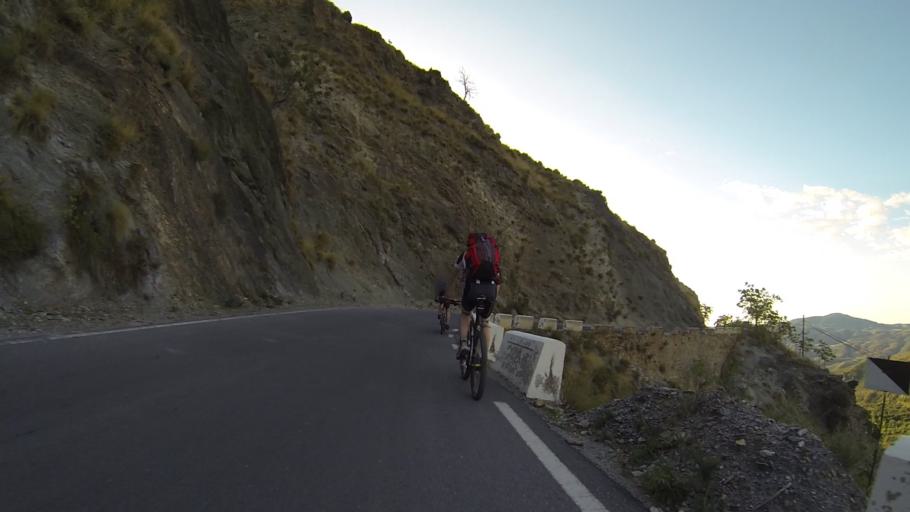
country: ES
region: Andalusia
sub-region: Provincia de Granada
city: Berchules
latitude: 36.9844
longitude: -3.1491
